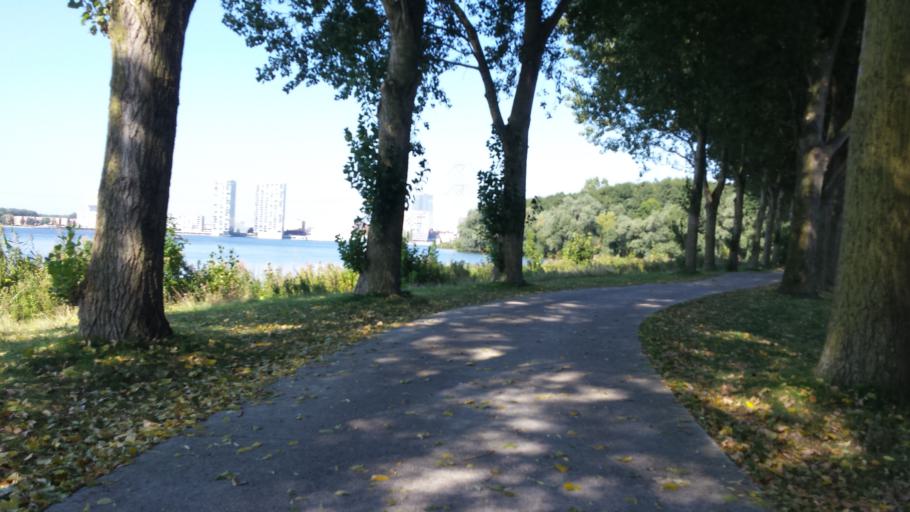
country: NL
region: Flevoland
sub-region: Gemeente Almere
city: Almere Stad
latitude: 52.3584
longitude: 5.2239
